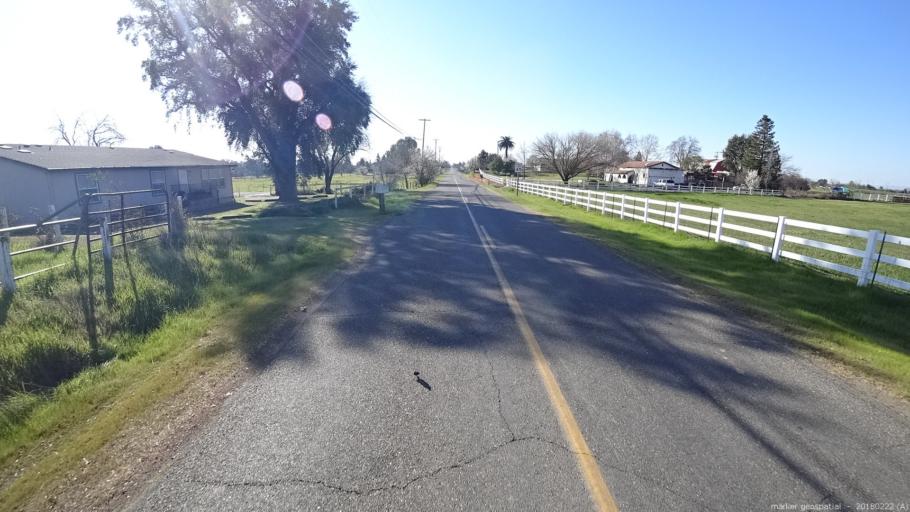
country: US
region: California
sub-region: Sacramento County
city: Elverta
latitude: 38.7321
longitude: -121.4576
